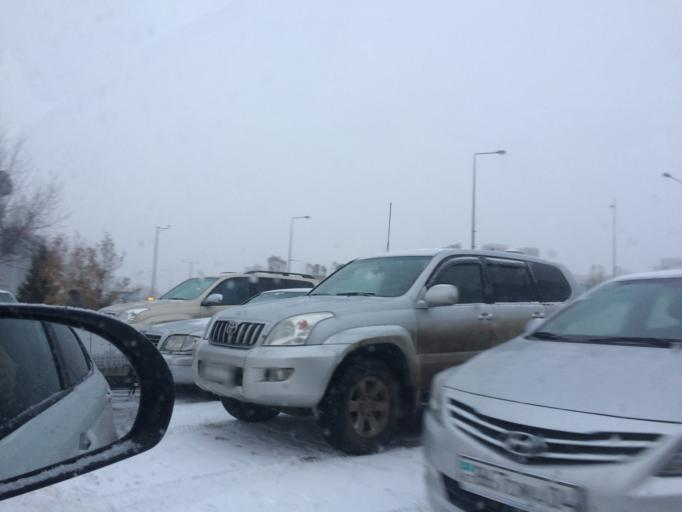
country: KZ
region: Astana Qalasy
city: Astana
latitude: 51.1325
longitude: 71.4138
